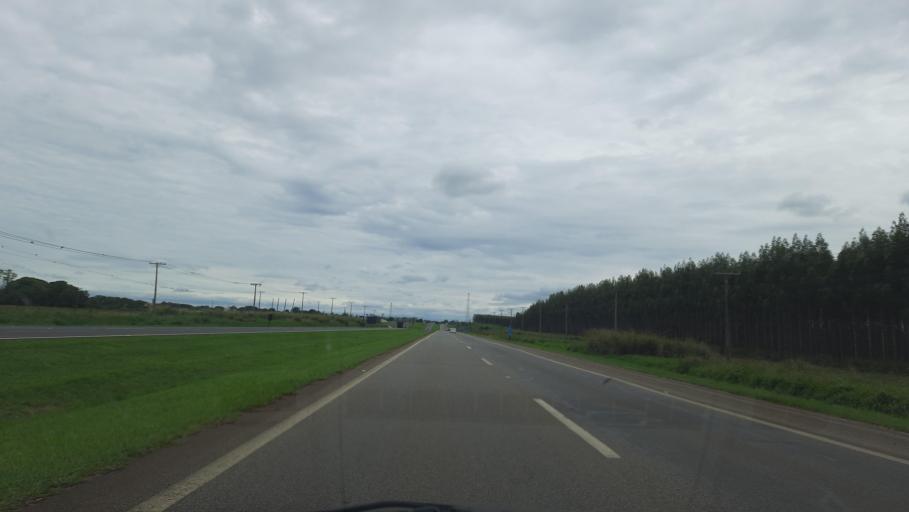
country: BR
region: Sao Paulo
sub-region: Moji-Guacu
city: Mogi-Gaucu
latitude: -22.3289
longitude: -46.9608
